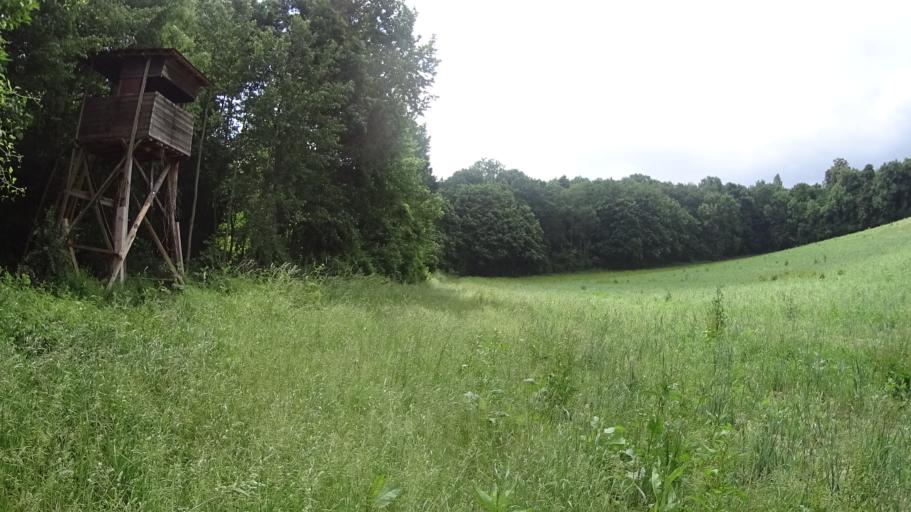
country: DE
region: Lower Saxony
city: Giesen
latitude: 52.1507
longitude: 9.8980
